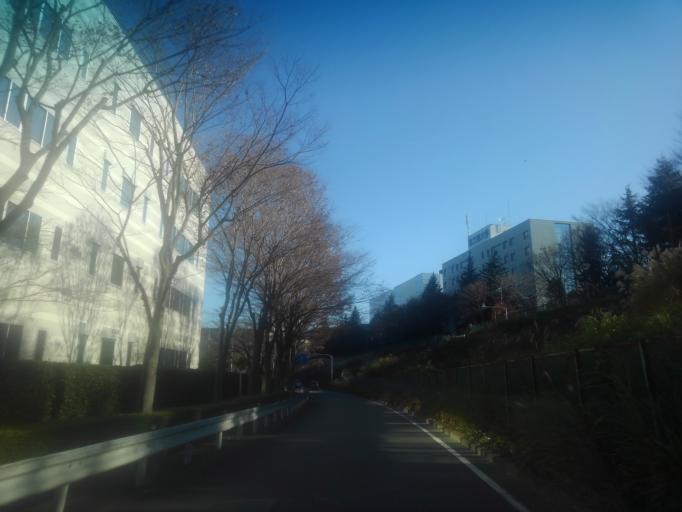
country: JP
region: Tokyo
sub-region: Machida-shi
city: Machida
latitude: 35.6121
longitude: 139.4469
